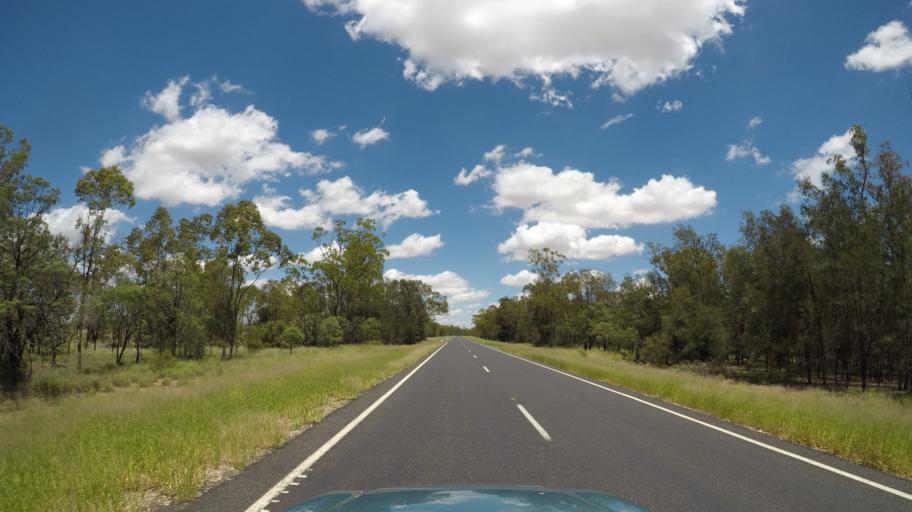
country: AU
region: Queensland
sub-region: Goondiwindi
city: Goondiwindi
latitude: -28.1718
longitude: 150.5767
